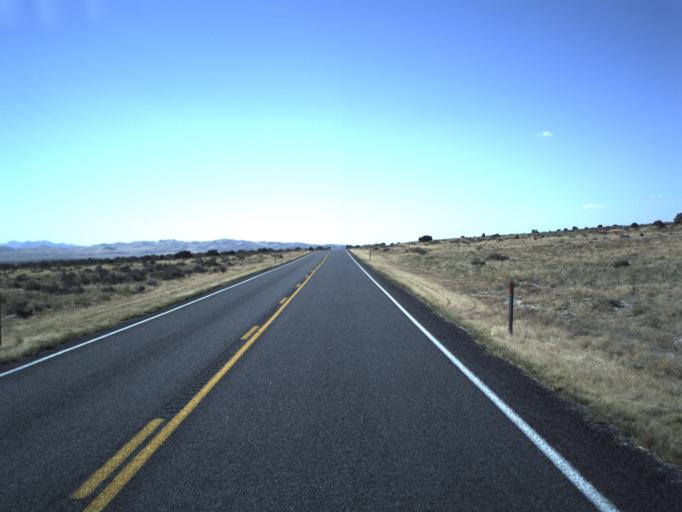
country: US
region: Utah
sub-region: Beaver County
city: Milford
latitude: 38.8458
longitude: -112.8439
